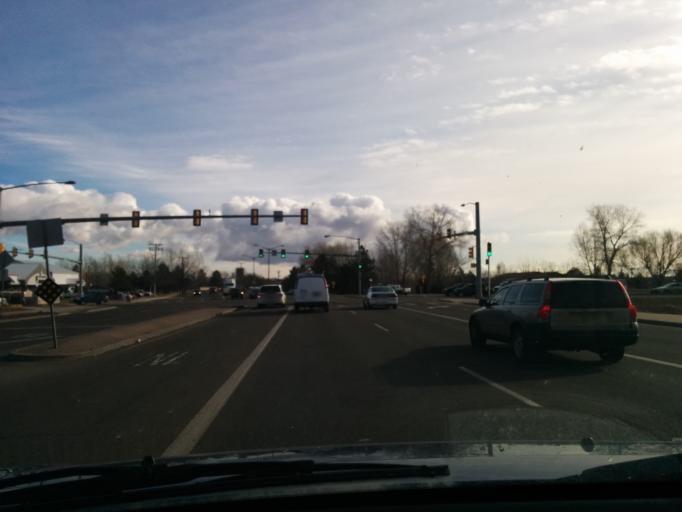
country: US
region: Colorado
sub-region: Larimer County
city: Fort Collins
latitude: 40.5671
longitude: -105.0402
